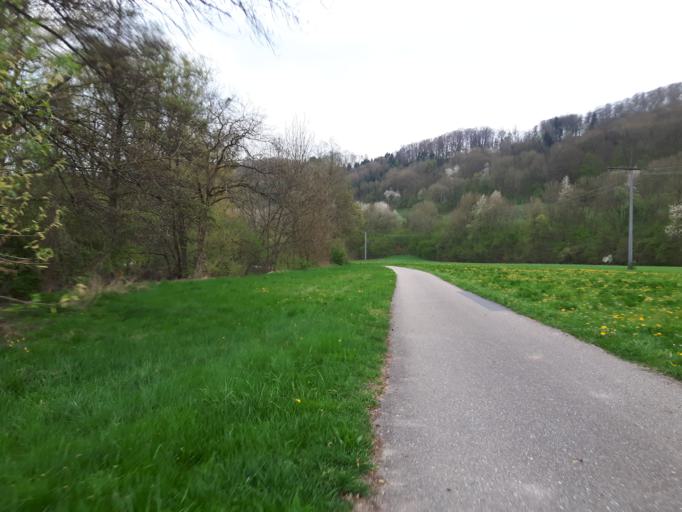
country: DE
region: Baden-Wuerttemberg
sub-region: Regierungsbezirk Stuttgart
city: Weissbach
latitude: 49.2904
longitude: 9.5997
